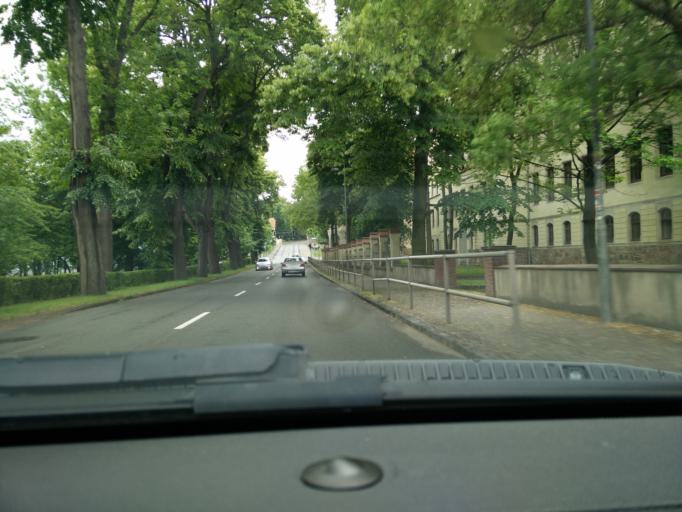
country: DE
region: Saxony
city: Grimma
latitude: 51.2317
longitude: 12.7228
